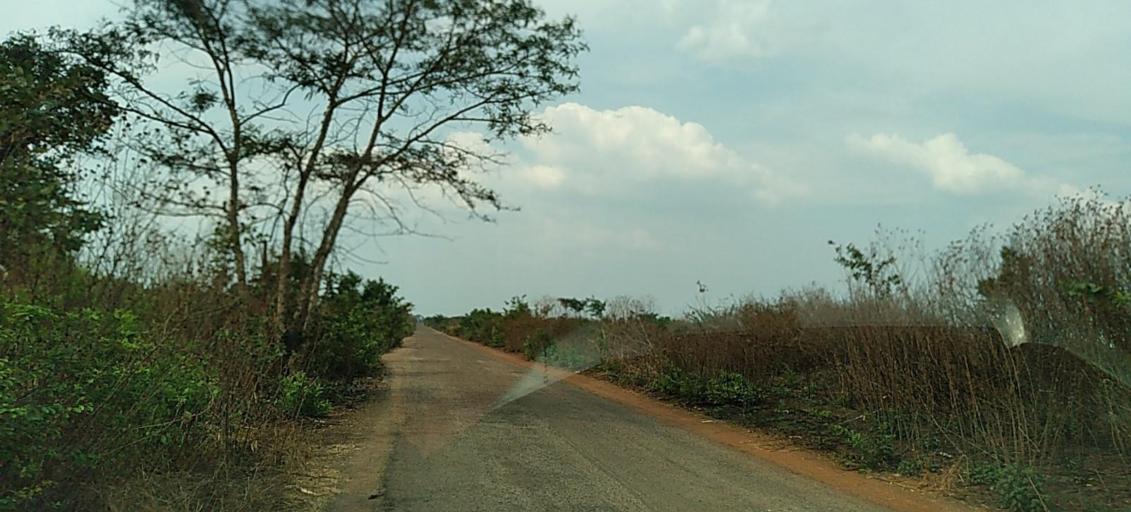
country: ZM
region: Copperbelt
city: Chililabombwe
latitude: -12.3891
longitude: 27.8078
